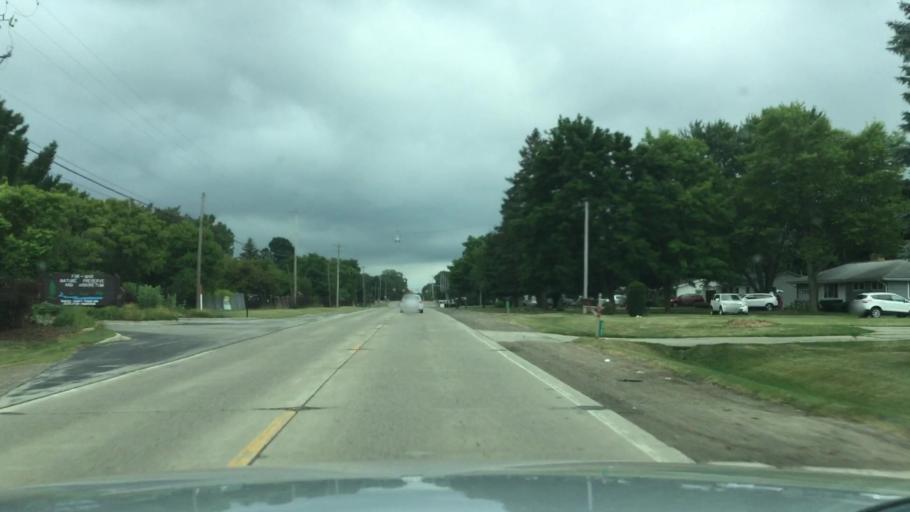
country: US
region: Michigan
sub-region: Genesee County
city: Burton
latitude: 43.0372
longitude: -83.6156
